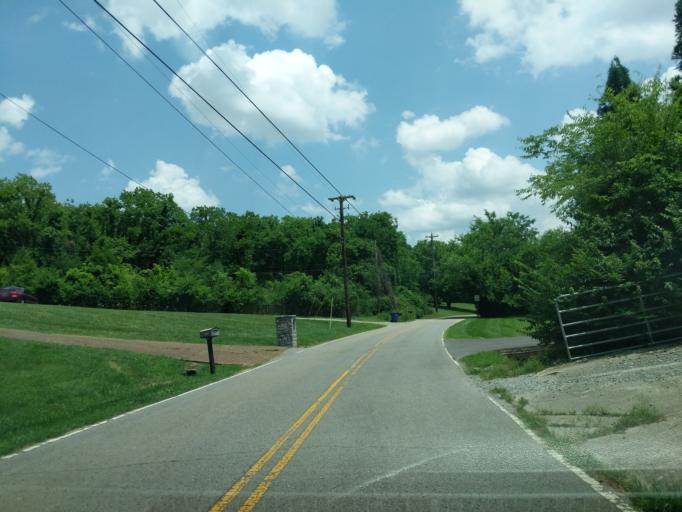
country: US
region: Tennessee
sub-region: Davidson County
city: Goodlettsville
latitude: 36.3138
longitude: -86.7350
